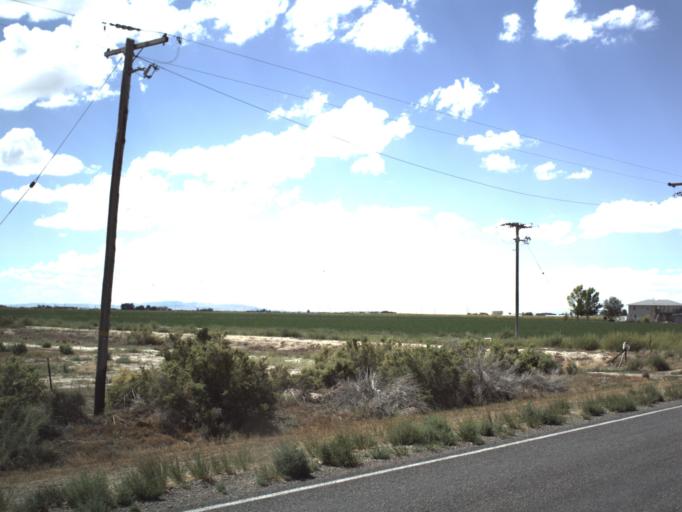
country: US
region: Utah
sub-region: Millard County
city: Delta
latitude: 39.3529
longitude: -112.5358
